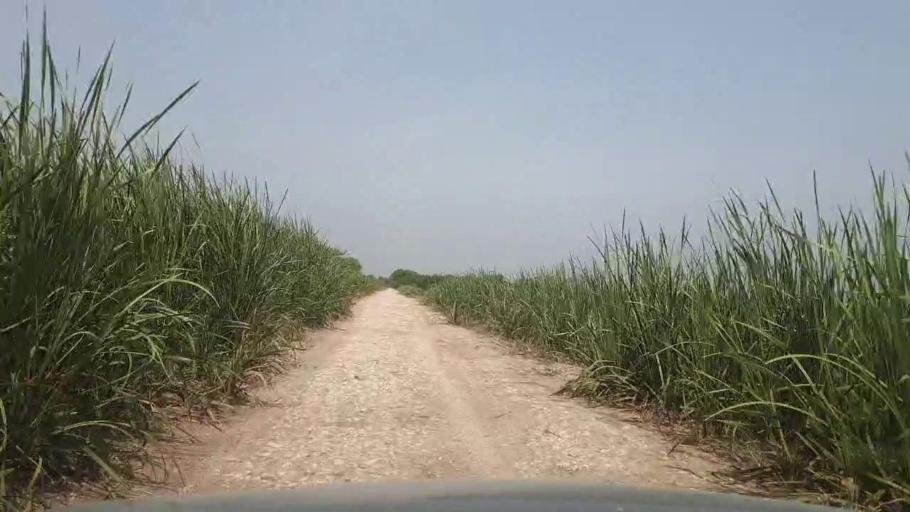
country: PK
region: Sindh
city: Garhi Yasin
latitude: 27.9430
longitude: 68.4301
